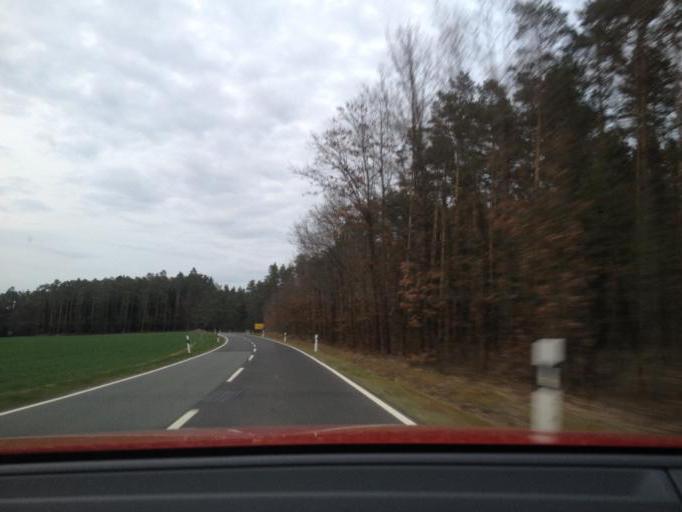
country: DE
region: Bavaria
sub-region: Upper Palatinate
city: Schlammersdorf
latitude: 49.7756
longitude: 11.7713
